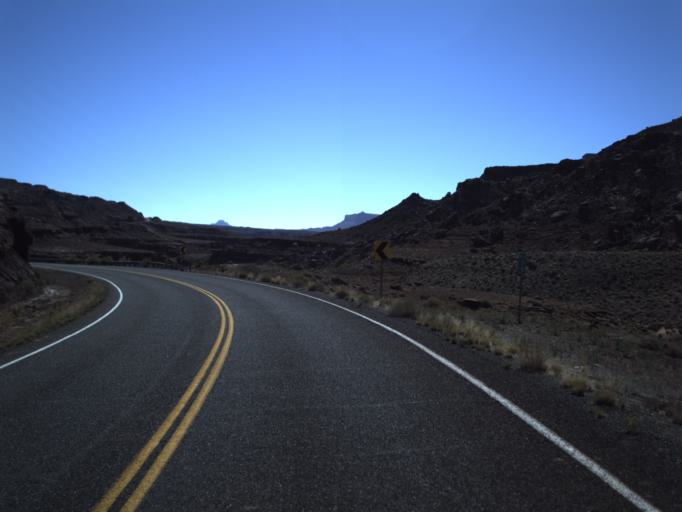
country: US
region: Utah
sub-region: San Juan County
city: Blanding
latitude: 37.8946
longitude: -110.4455
